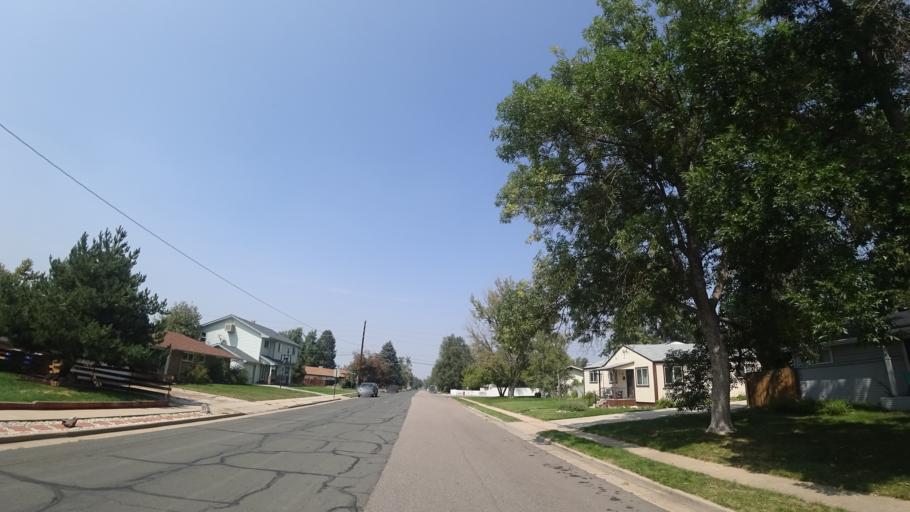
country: US
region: Colorado
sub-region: Arapahoe County
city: Englewood
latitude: 39.6287
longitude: -104.9973
